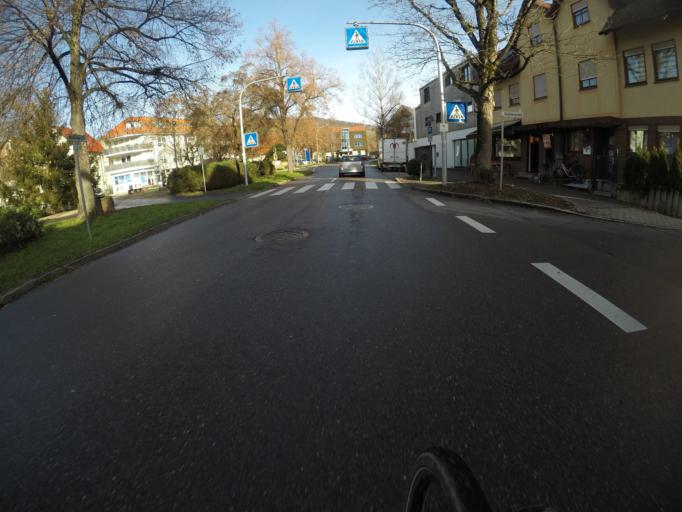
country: DE
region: Baden-Wuerttemberg
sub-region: Regierungsbezirk Stuttgart
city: Korb
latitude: 48.8421
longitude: 9.3618
